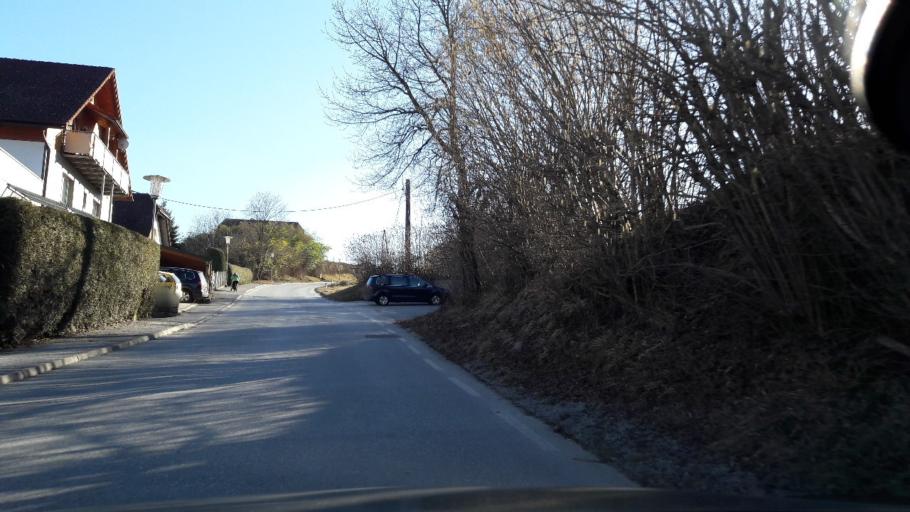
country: AT
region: Styria
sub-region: Politischer Bezirk Graz-Umgebung
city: Eisbach
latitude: 47.1339
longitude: 15.2878
